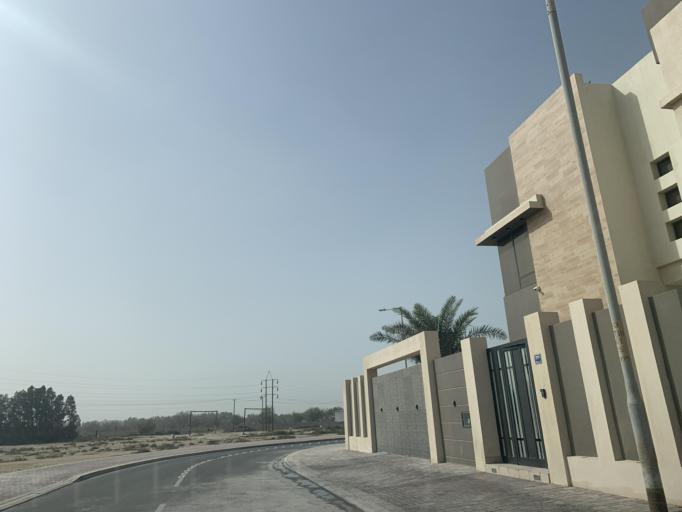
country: BH
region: Northern
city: Madinat `Isa
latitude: 26.1610
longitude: 50.5363
